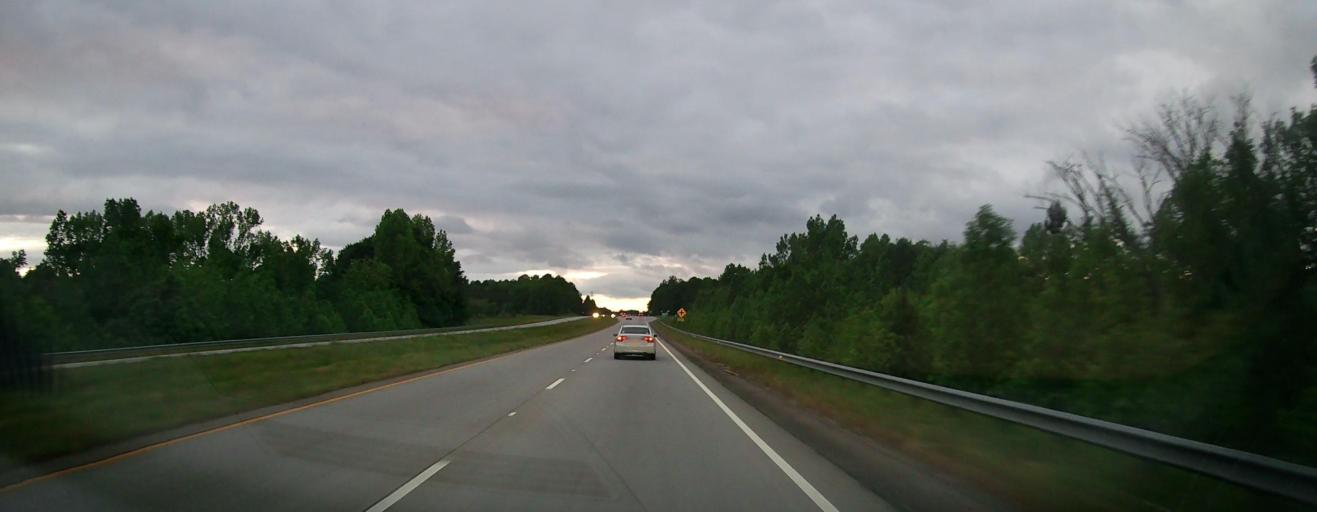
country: US
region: Georgia
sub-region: Jackson County
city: Arcade
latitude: 34.0885
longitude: -83.5816
